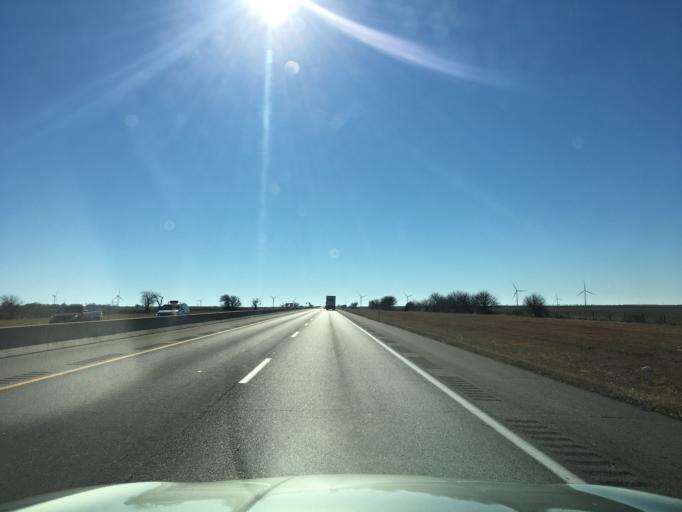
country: US
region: Kansas
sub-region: Sumner County
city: Wellington
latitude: 37.1810
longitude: -97.3396
